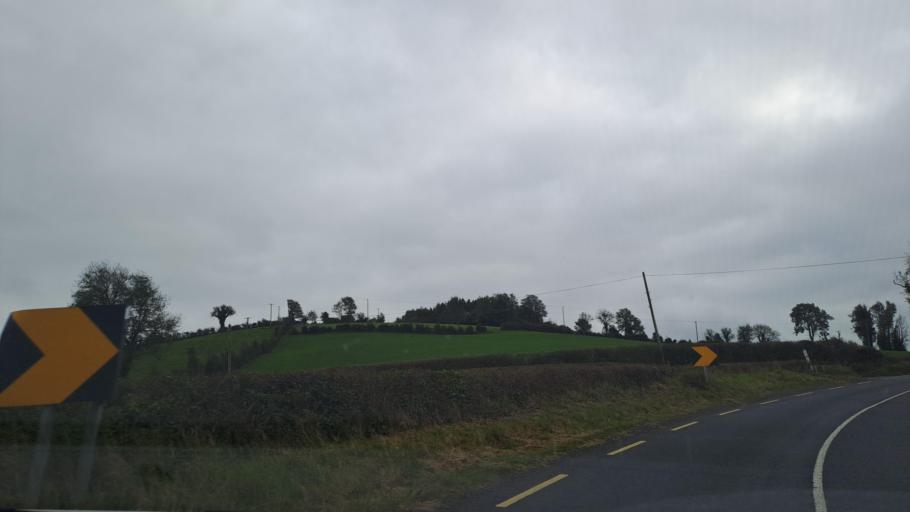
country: IE
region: Ulster
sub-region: An Cabhan
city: Cootehill
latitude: 54.0392
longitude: -7.0424
